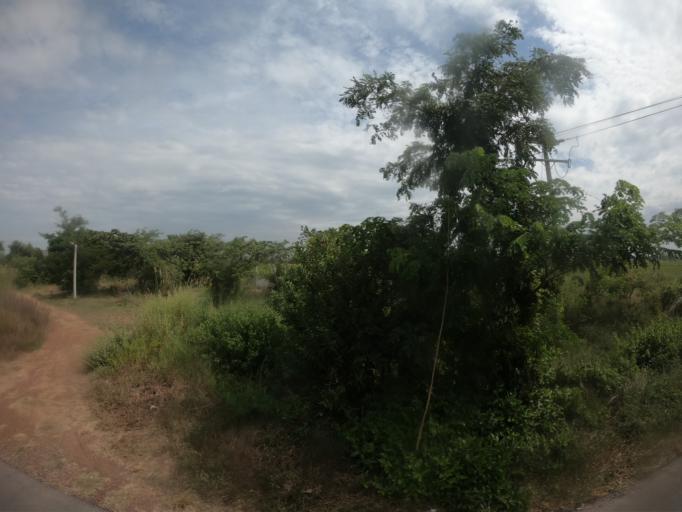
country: TH
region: Maha Sarakham
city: Chiang Yuen
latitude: 16.3730
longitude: 103.1055
